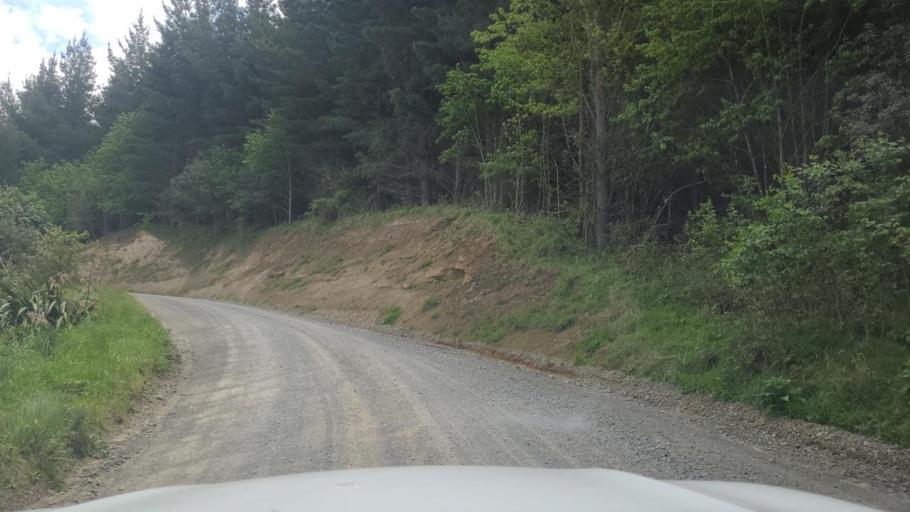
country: NZ
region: Hawke's Bay
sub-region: Napier City
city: Taradale
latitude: -39.2733
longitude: 176.6709
